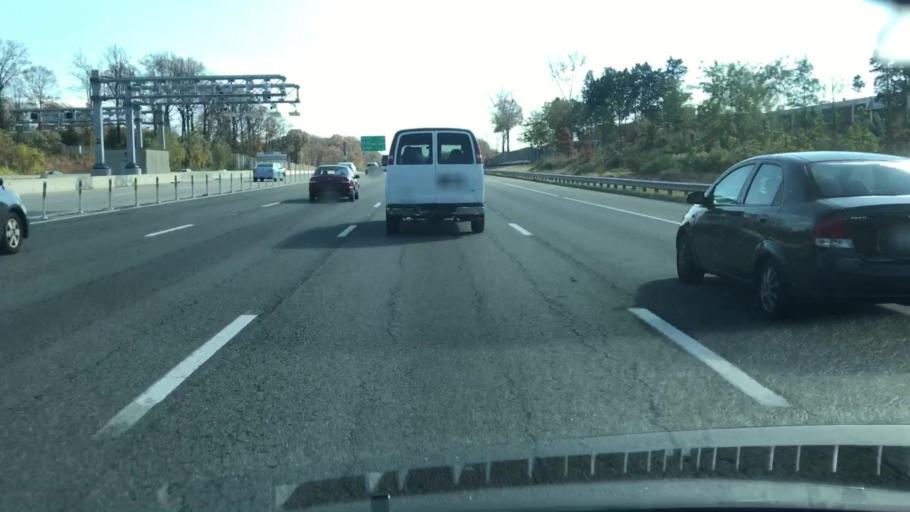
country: US
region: Virginia
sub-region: Fairfax County
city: Ravensworth
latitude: 38.8107
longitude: -77.2178
